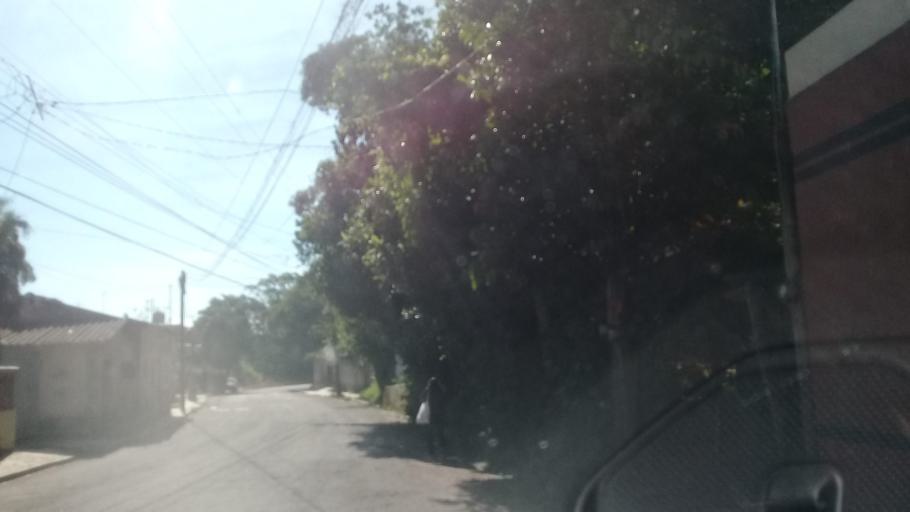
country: MX
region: Veracruz
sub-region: Tlalnelhuayocan
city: Guadalupe Victoria
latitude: 19.5503
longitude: -96.9521
